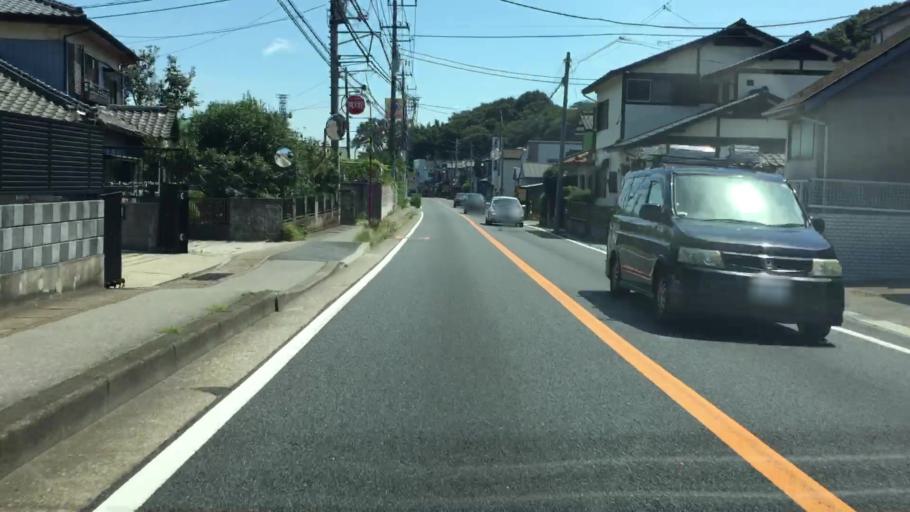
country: JP
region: Chiba
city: Matsudo
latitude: 35.7716
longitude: 139.9184
